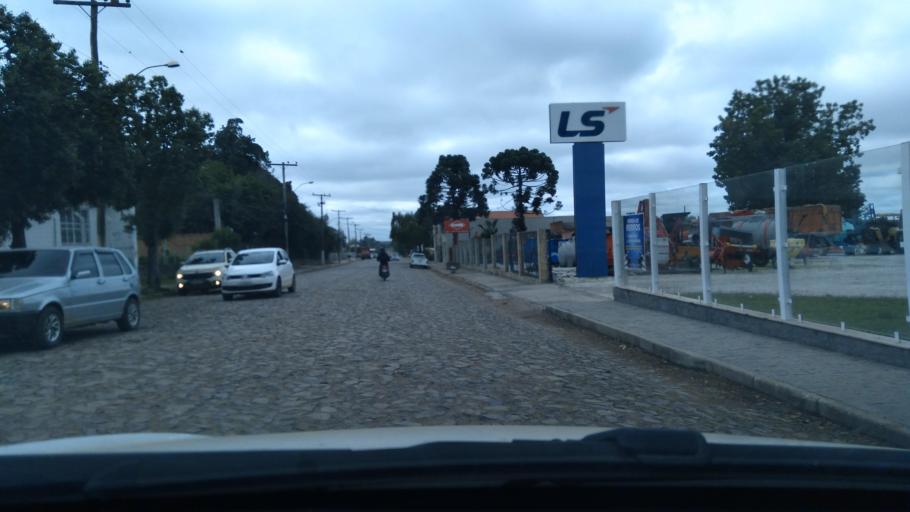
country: BR
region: Rio Grande do Sul
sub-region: Dom Pedrito
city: Dom Pedrito
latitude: -30.9666
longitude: -54.6732
